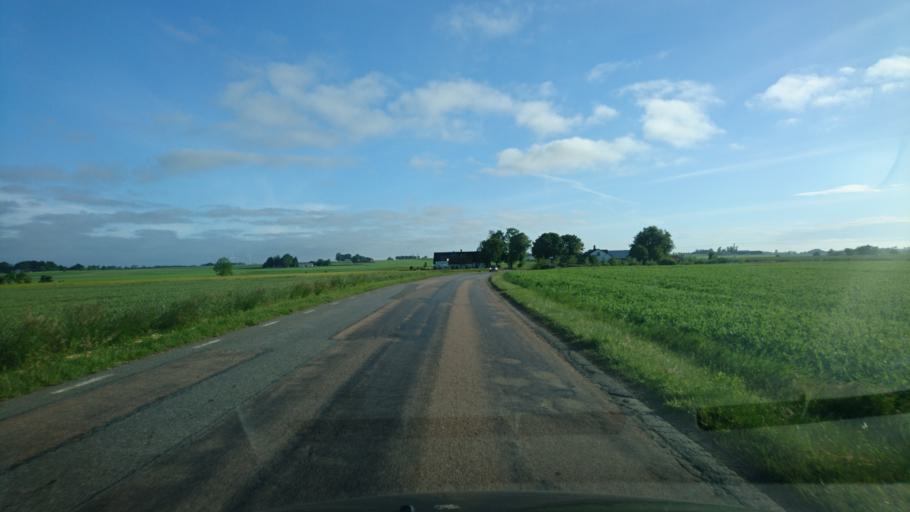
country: SE
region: Skane
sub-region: Tomelilla Kommun
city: Tomelilla
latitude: 55.4697
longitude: 14.0977
